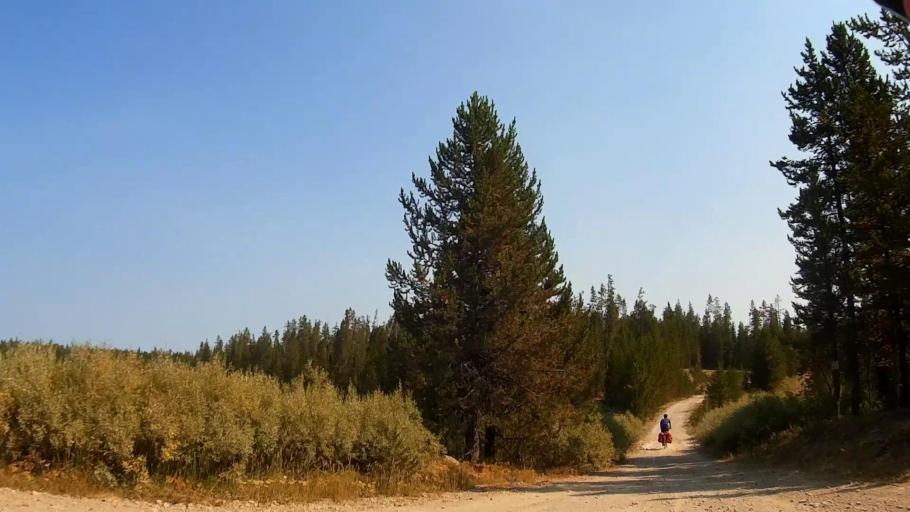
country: US
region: Montana
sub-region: Gallatin County
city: West Yellowstone
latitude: 44.5768
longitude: -111.1817
